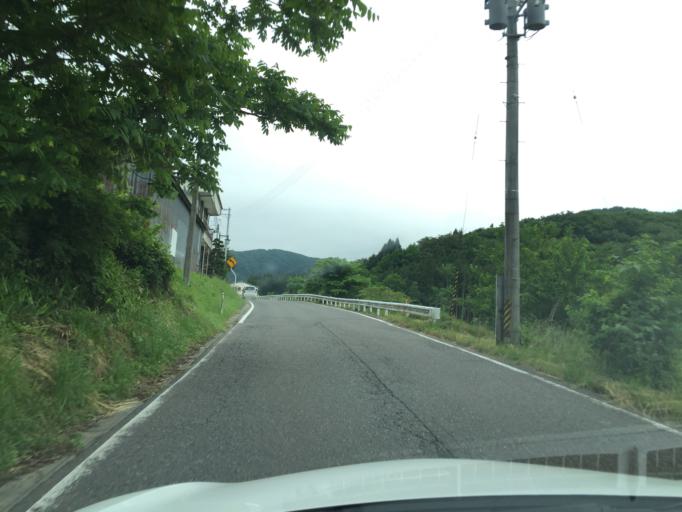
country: JP
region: Fukushima
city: Funehikimachi-funehiki
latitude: 37.3692
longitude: 140.6385
